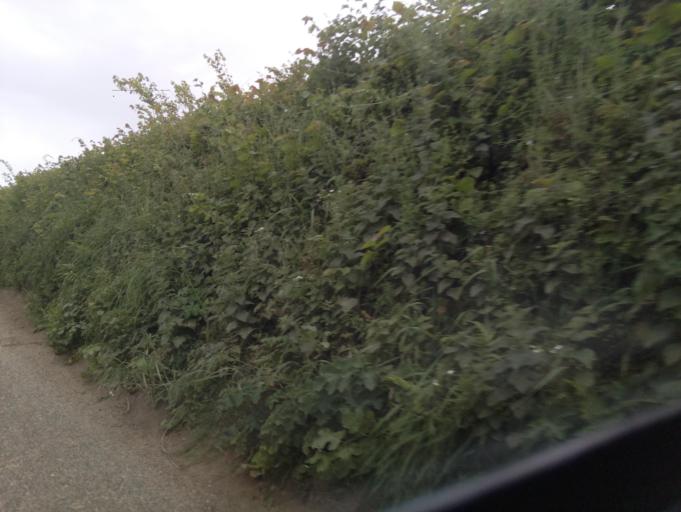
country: GB
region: England
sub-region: Devon
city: Dartmouth
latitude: 50.3193
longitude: -3.6353
